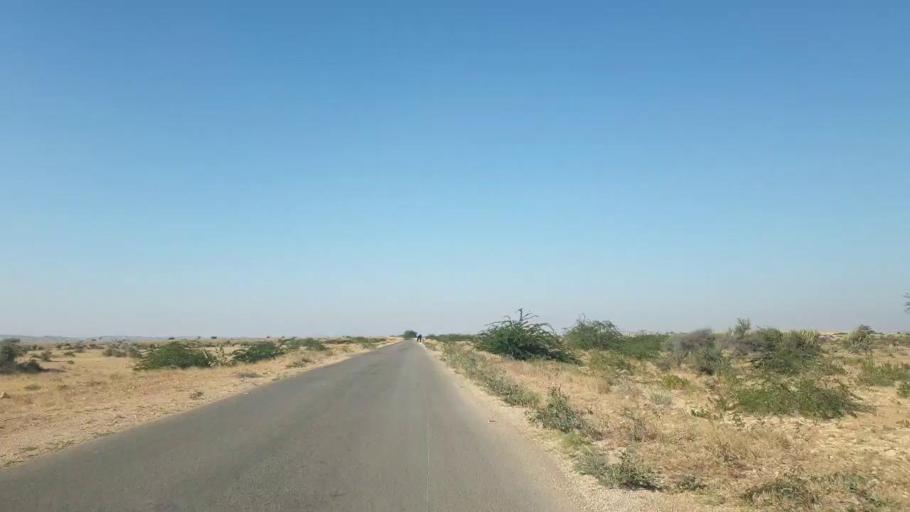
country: PK
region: Sindh
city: Malir Cantonment
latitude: 25.2528
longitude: 67.6031
